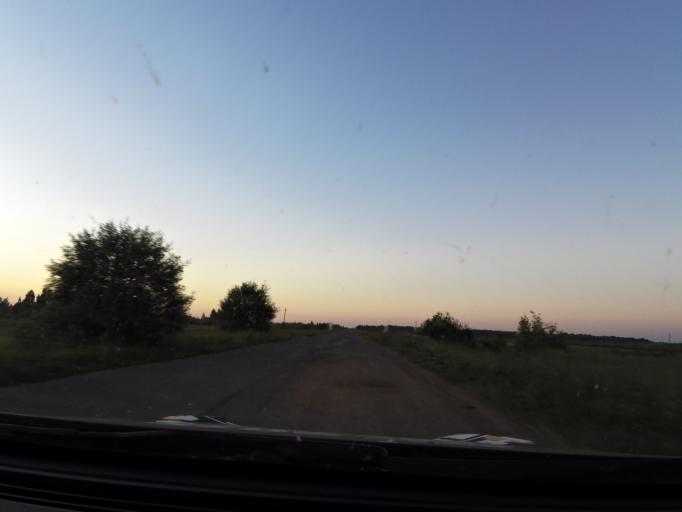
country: RU
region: Kostroma
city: Buy
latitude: 58.3748
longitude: 41.2105
